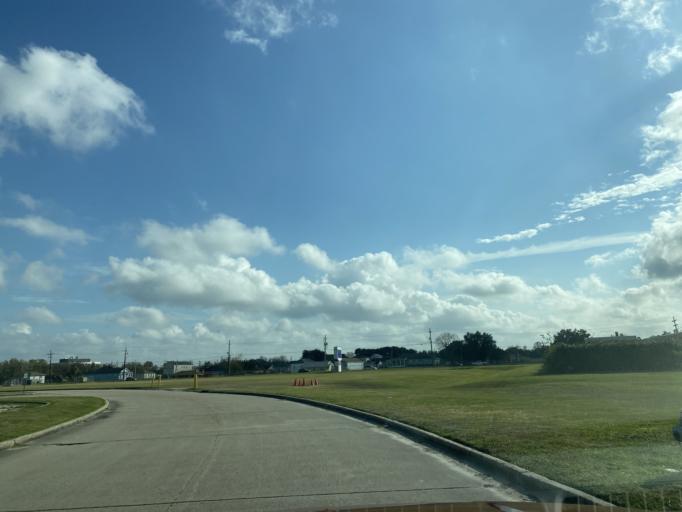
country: US
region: Louisiana
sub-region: Orleans Parish
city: New Orleans
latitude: 30.0284
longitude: -90.0510
